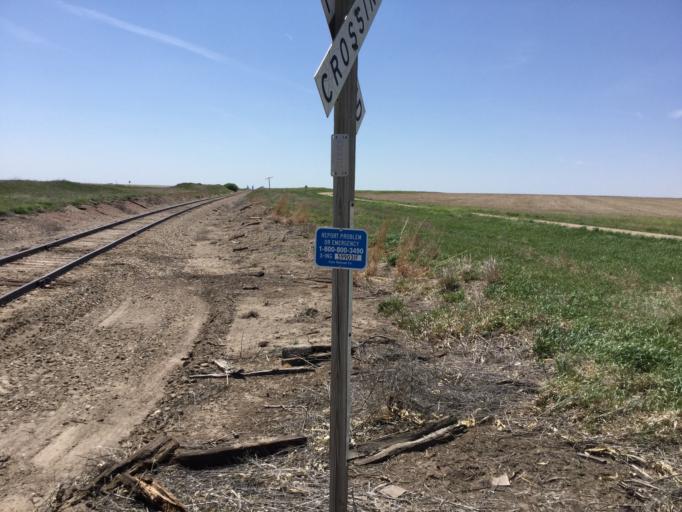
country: US
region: Kansas
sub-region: Decatur County
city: Oberlin
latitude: 39.6406
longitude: -100.3674
